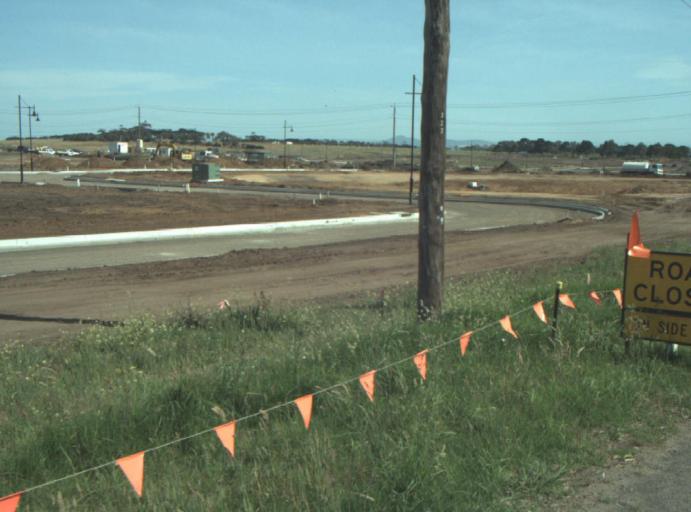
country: AU
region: Victoria
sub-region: Greater Geelong
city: Clifton Springs
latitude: -38.1757
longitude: 144.5518
